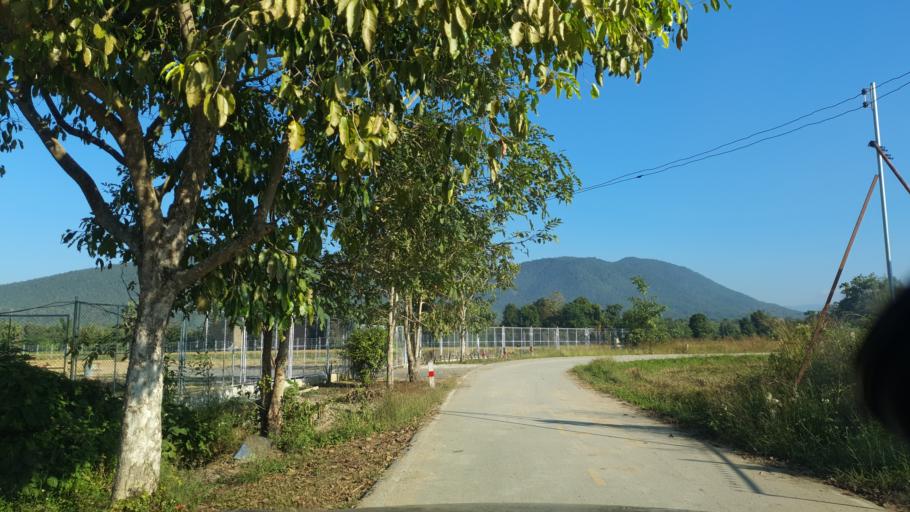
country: TH
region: Chiang Mai
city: Mae On
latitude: 18.7330
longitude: 99.2141
